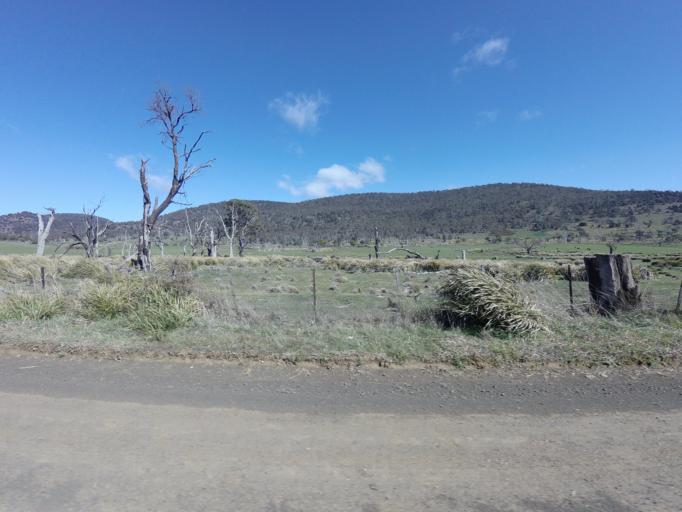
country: AU
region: Tasmania
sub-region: Northern Midlands
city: Evandale
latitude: -41.9367
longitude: 147.4205
